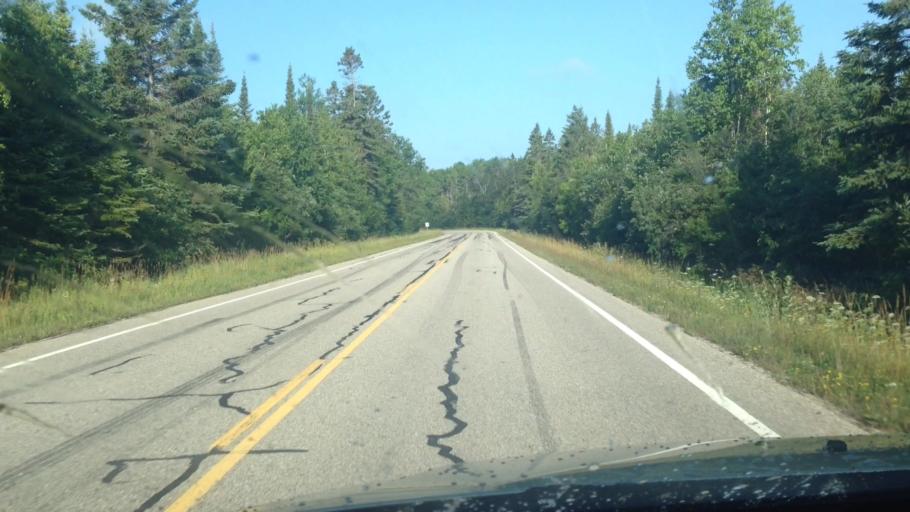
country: US
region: Michigan
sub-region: Mackinac County
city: Saint Ignace
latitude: 45.8931
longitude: -84.7826
